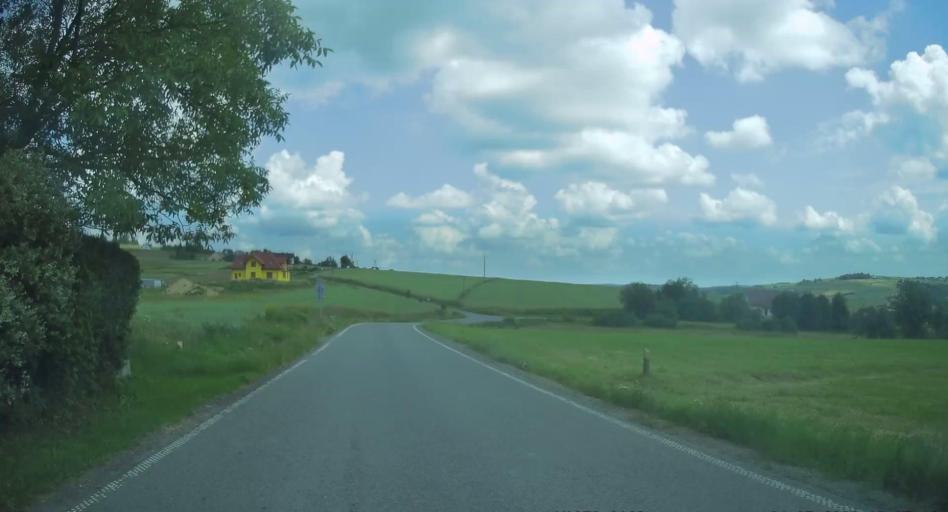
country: PL
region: Lesser Poland Voivodeship
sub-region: Powiat nowosadecki
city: Korzenna
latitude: 49.7083
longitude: 20.7647
